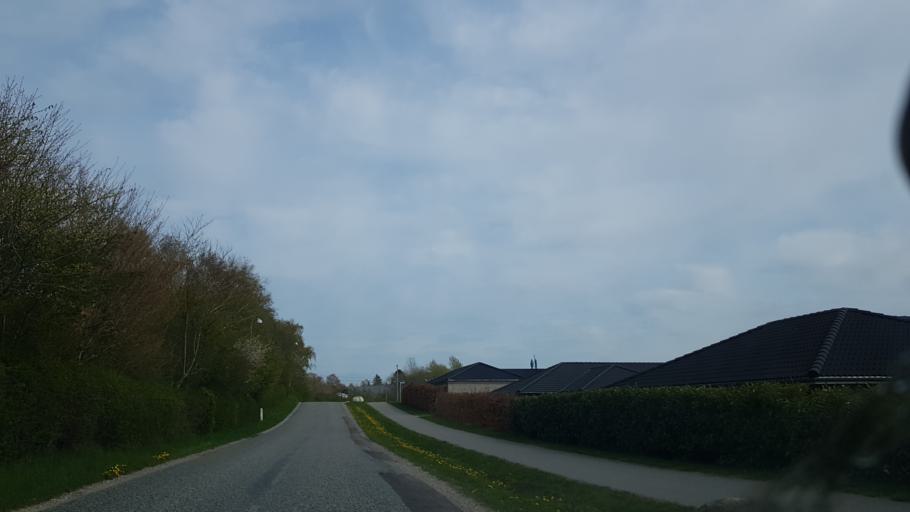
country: DK
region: Capital Region
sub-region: Allerod Kommune
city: Lillerod
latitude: 55.8840
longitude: 12.3430
